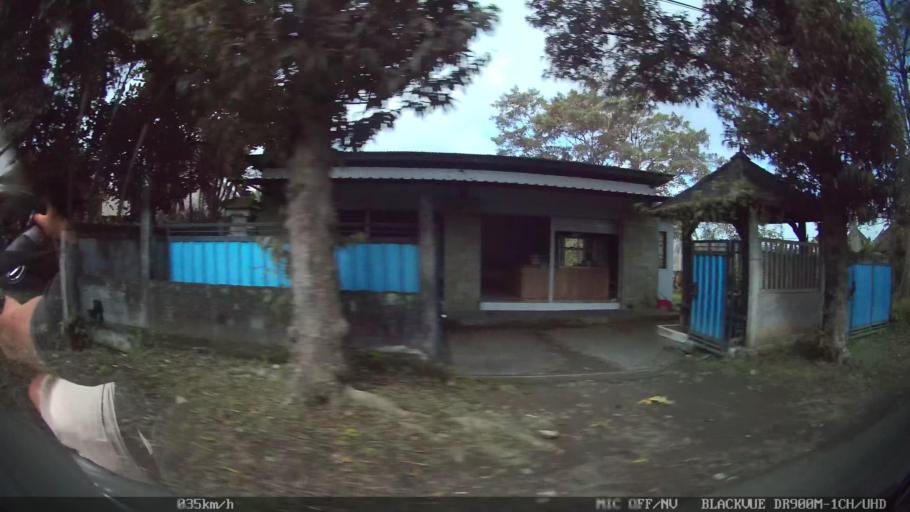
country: ID
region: Bali
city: Banjar Pesalakan
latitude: -8.5152
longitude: 115.3021
